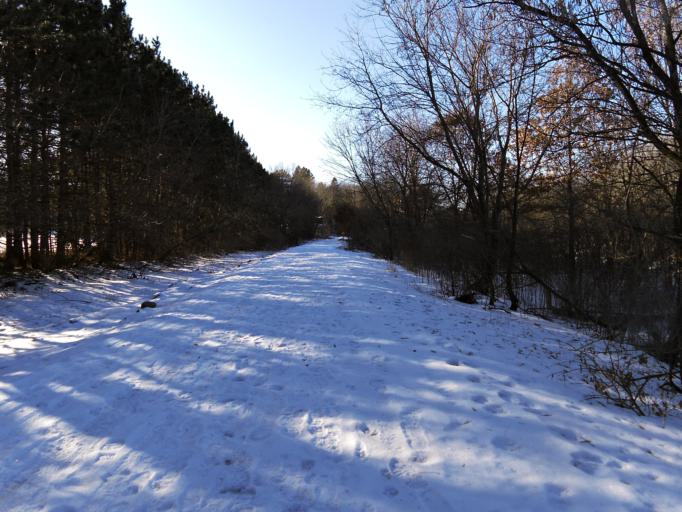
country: US
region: Minnesota
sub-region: Washington County
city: Grant
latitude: 45.0722
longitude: -92.8662
